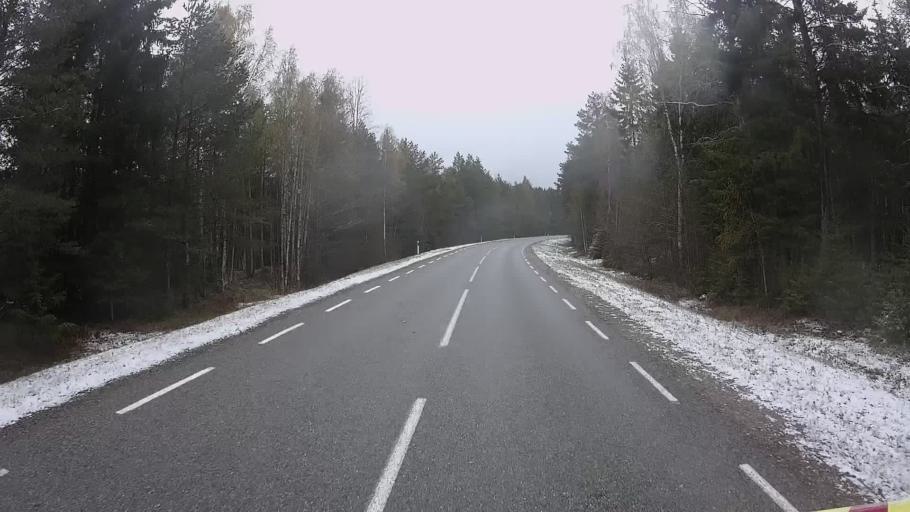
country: EE
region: Hiiumaa
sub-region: Kaerdla linn
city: Kardla
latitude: 59.0279
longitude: 22.6724
